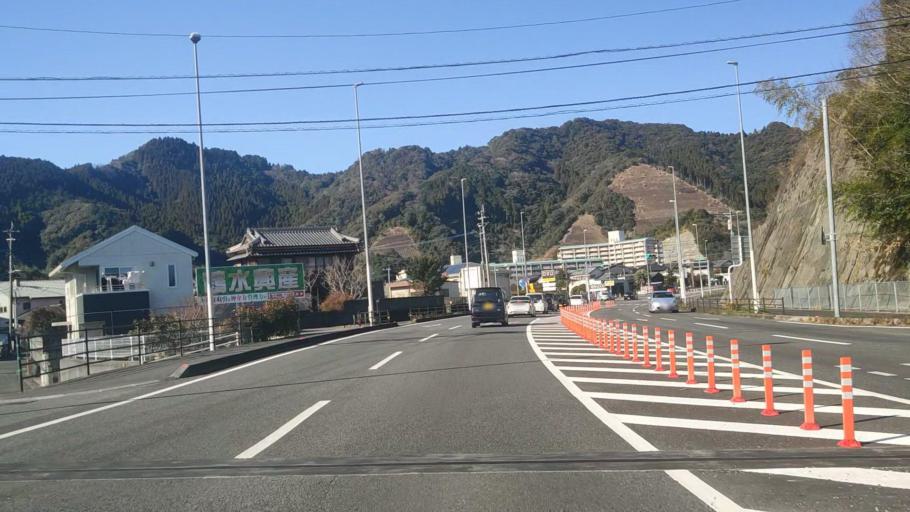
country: JP
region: Oita
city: Saiki
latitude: 32.9619
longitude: 131.8629
